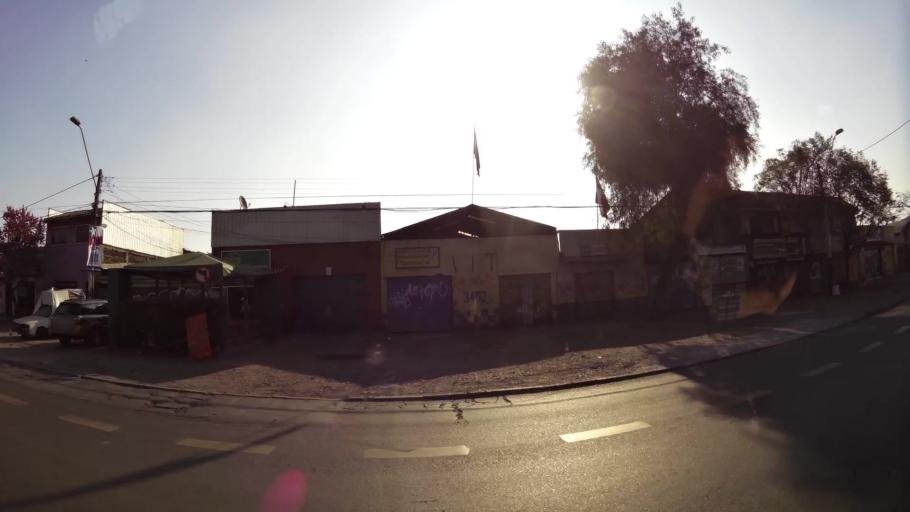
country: CL
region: Santiago Metropolitan
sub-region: Provincia de Santiago
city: Santiago
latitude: -33.3947
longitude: -70.6427
